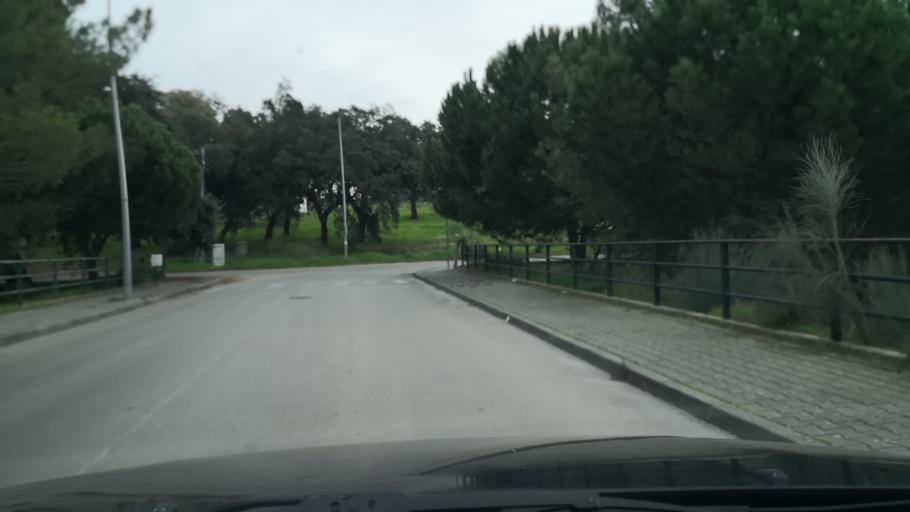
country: PT
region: Setubal
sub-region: Setubal
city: Setubal
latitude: 38.5489
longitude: -8.8833
